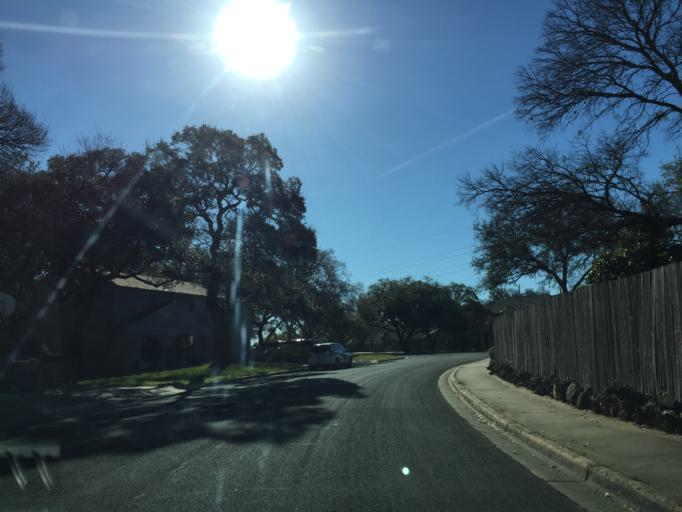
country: US
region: Texas
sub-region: Williamson County
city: Jollyville
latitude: 30.4066
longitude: -97.7331
